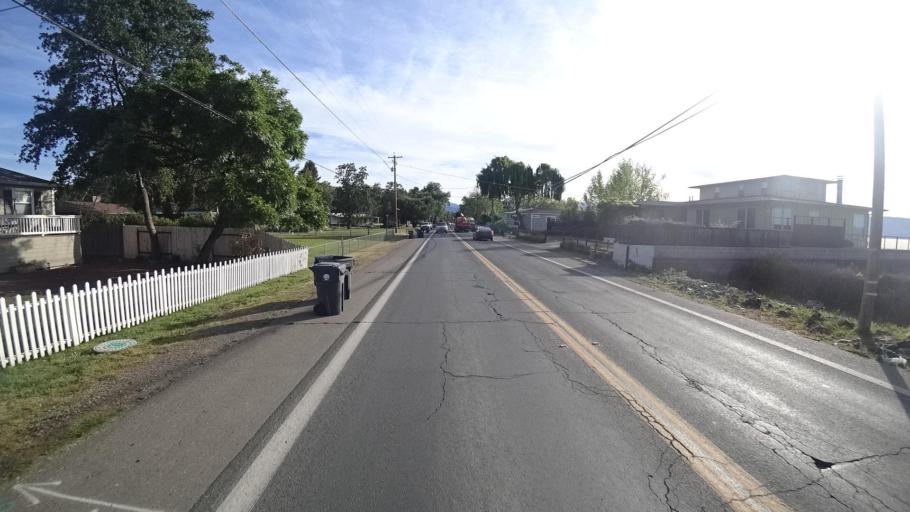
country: US
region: California
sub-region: Lake County
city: North Lakeport
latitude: 39.0752
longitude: -122.9113
